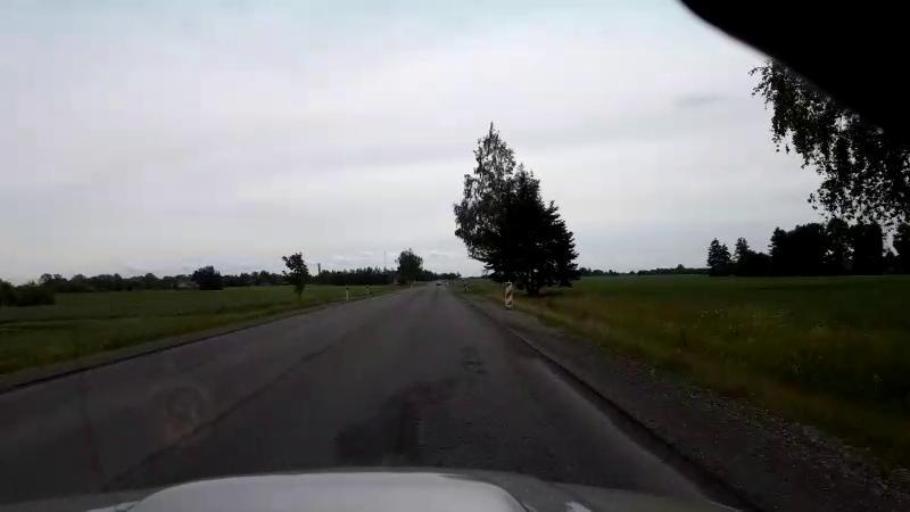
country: LV
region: Bauskas Rajons
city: Bauska
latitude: 56.3162
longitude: 24.3269
